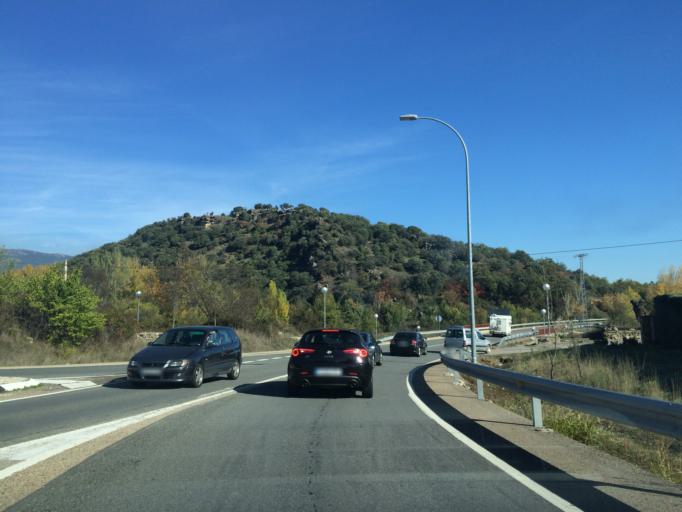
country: ES
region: Madrid
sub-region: Provincia de Madrid
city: Guadalix de la Sierra
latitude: 40.7875
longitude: -3.7062
